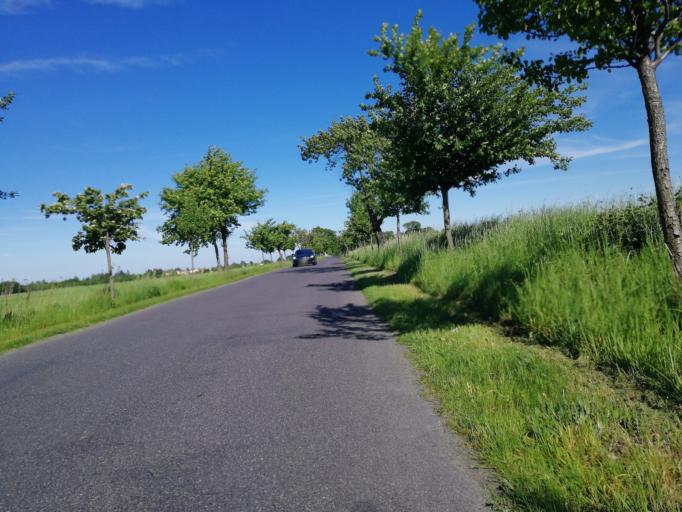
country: DE
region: Brandenburg
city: Calau
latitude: 51.7462
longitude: 13.9311
